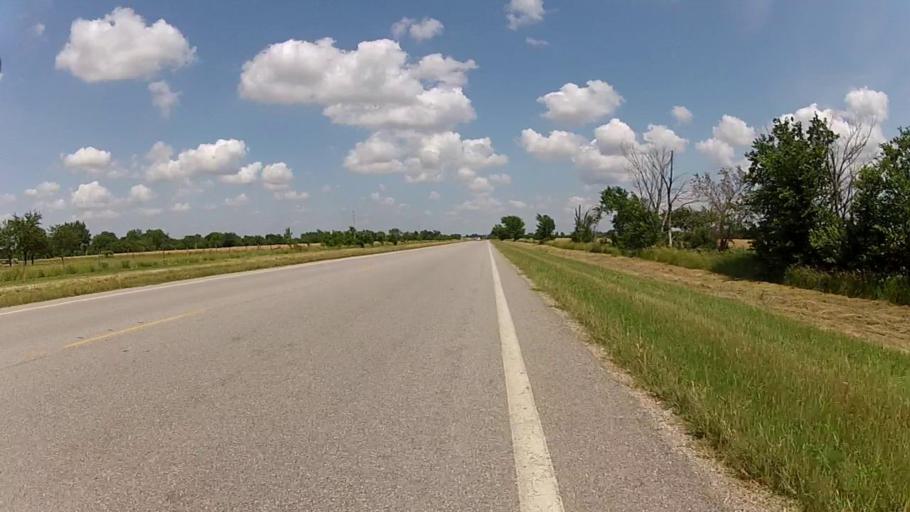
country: US
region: Kansas
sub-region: Labette County
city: Altamont
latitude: 37.1931
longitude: -95.2364
